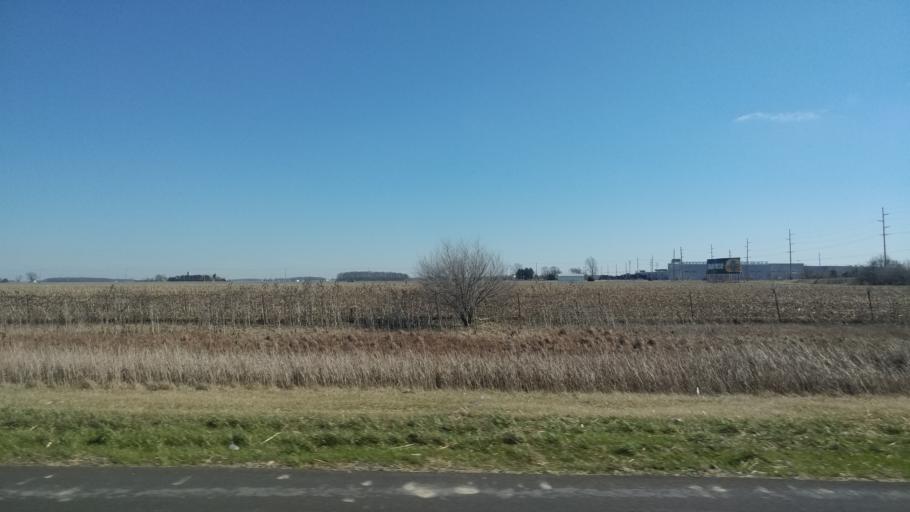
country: US
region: Ohio
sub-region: Wood County
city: Bowling Green
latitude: 41.3862
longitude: -83.6159
